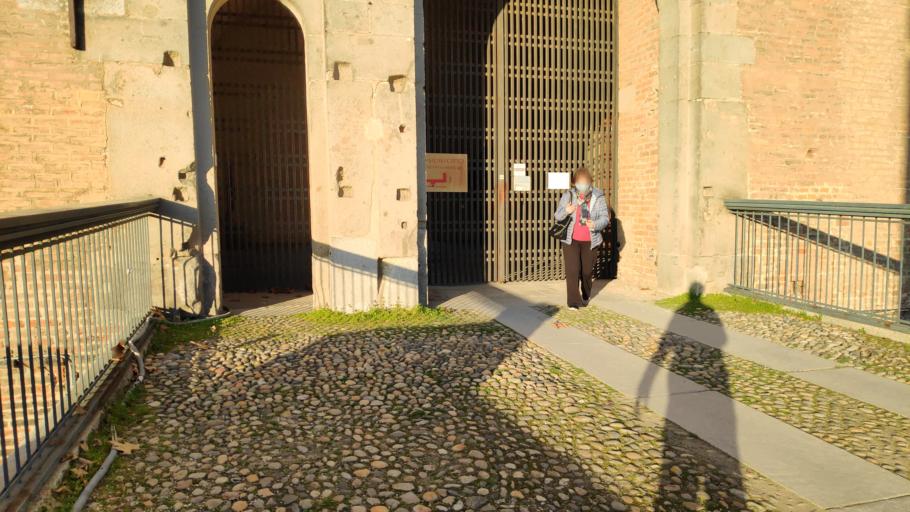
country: IT
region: Lombardy
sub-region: Provincia di Pavia
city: Pavia
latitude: 45.1900
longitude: 9.1582
